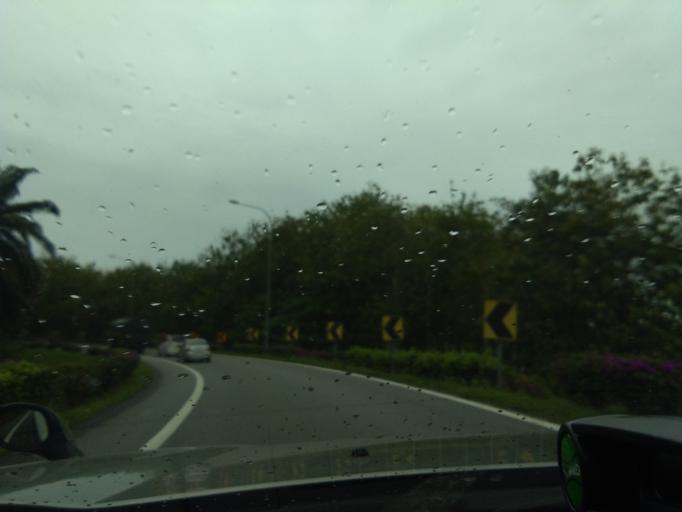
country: MY
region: Penang
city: Nibong Tebal
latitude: 5.1869
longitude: 100.4941
